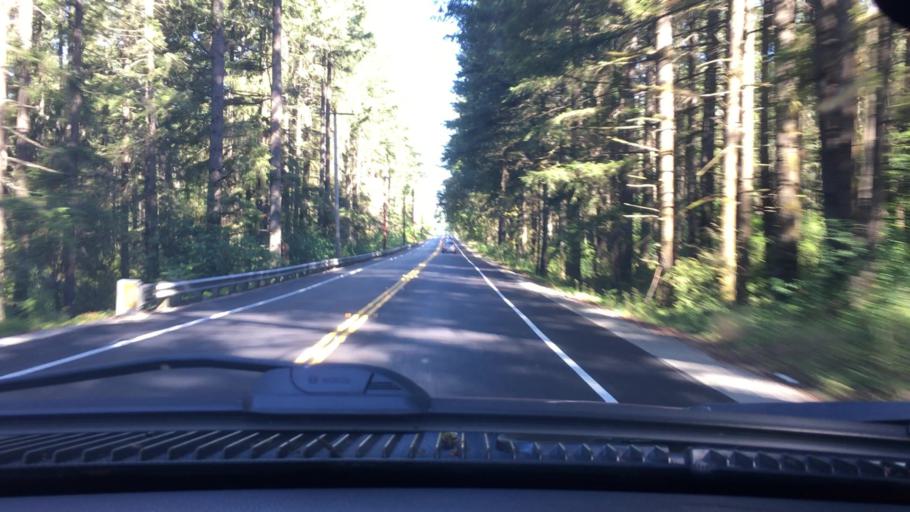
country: US
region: Washington
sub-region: King County
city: Lake Morton-Berrydale
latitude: 47.3187
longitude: -122.1035
